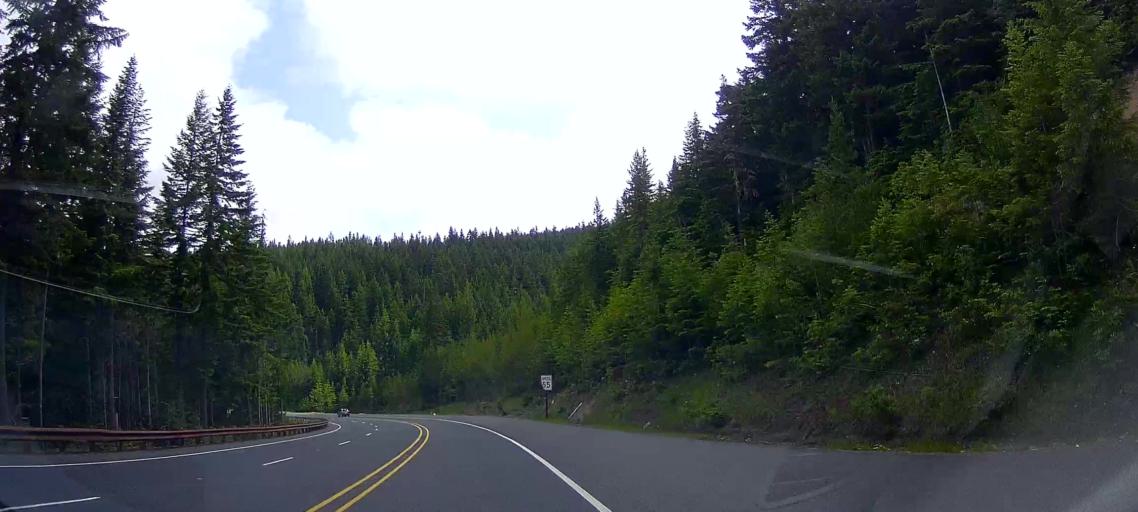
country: US
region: Oregon
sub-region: Clackamas County
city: Mount Hood Village
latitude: 45.2352
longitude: -121.6991
